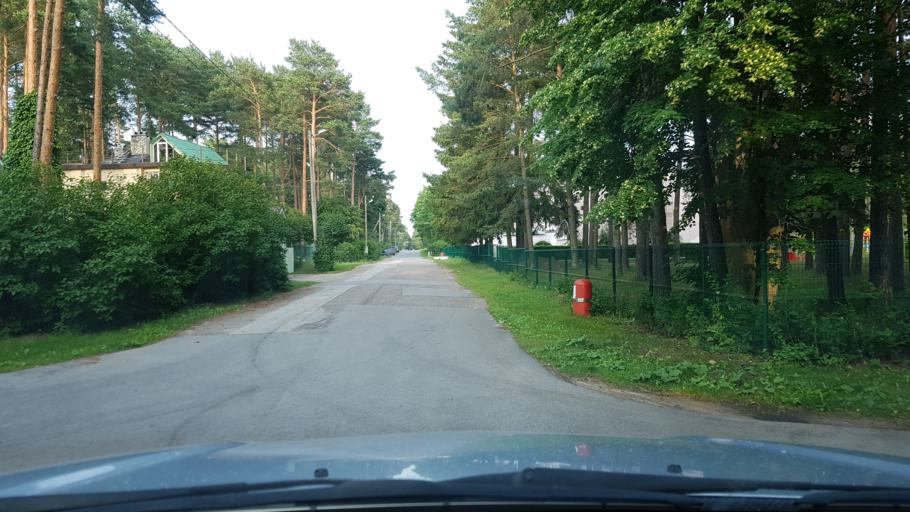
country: EE
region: Ida-Virumaa
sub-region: Narva-Joesuu linn
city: Narva-Joesuu
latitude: 59.4567
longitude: 28.0451
